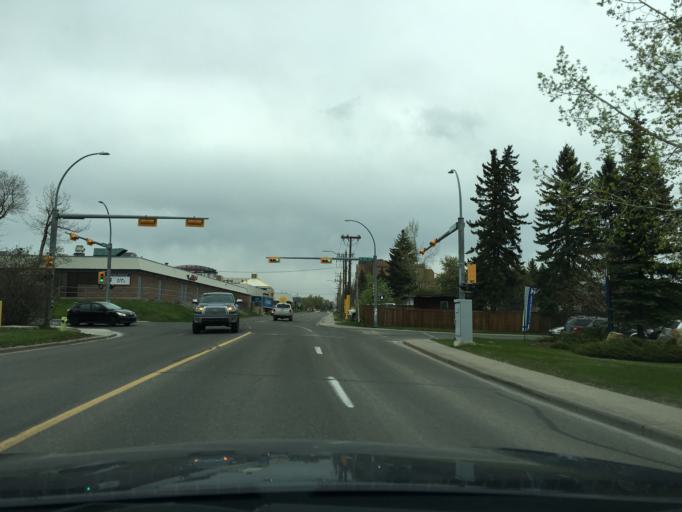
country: CA
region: Alberta
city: Calgary
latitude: 50.9682
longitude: -114.0686
